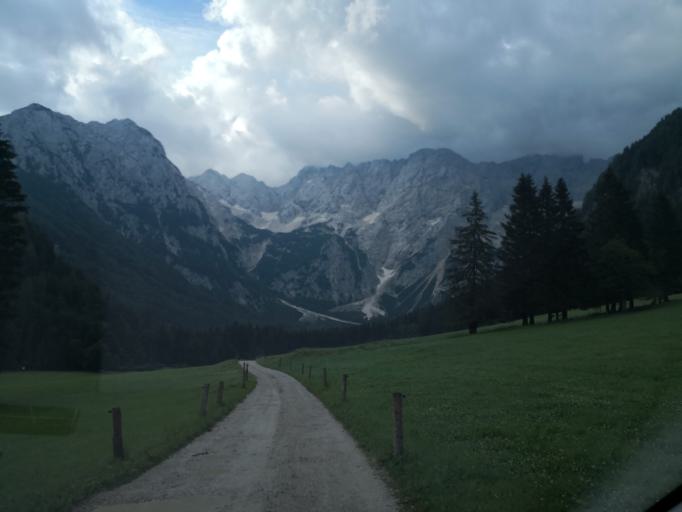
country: SI
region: Jezersko
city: Zgornje Jezersko
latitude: 46.3940
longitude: 14.5279
